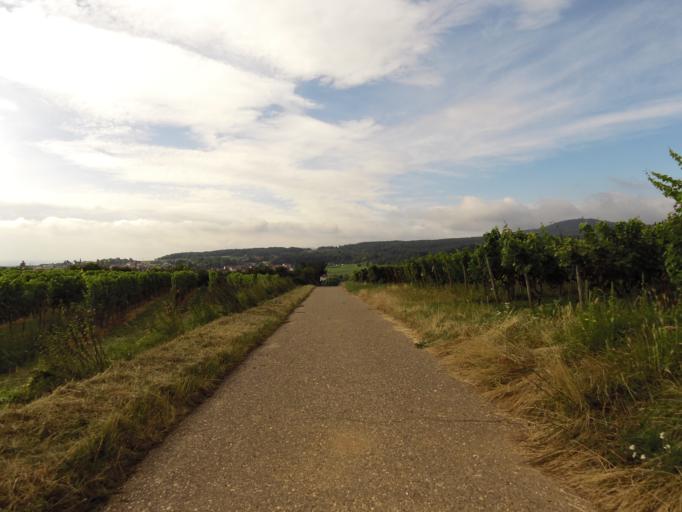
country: DE
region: Rheinland-Pfalz
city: Weisenheim am Berg
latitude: 49.5017
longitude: 8.1541
